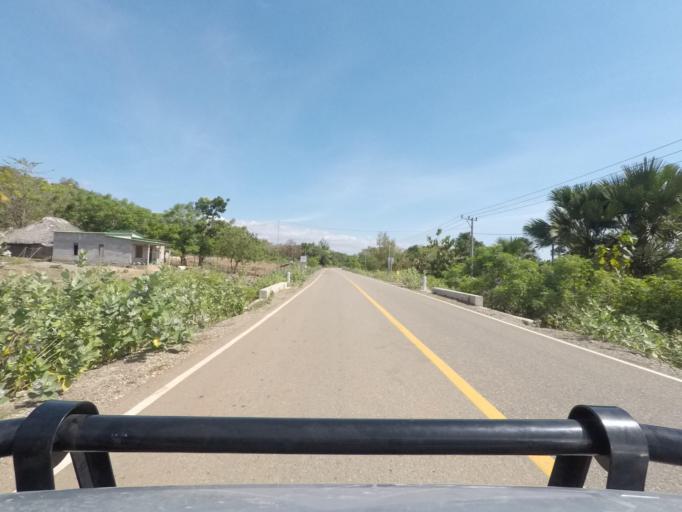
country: TL
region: Bobonaro
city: Maliana
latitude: -8.8856
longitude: 125.0262
